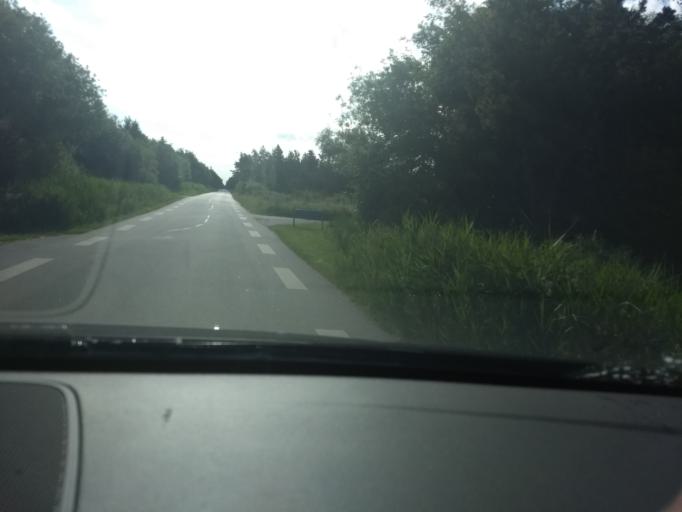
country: DE
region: Schleswig-Holstein
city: List
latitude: 55.1302
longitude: 8.5231
